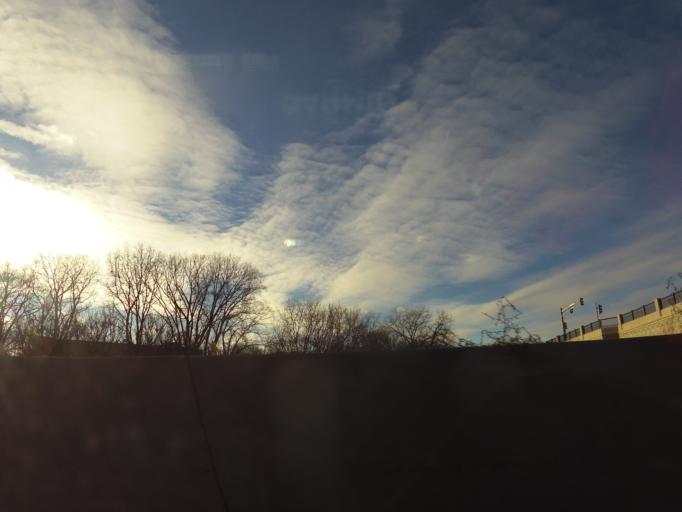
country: US
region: Minnesota
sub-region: Hennepin County
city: Richfield
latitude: 44.8650
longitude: -93.2987
